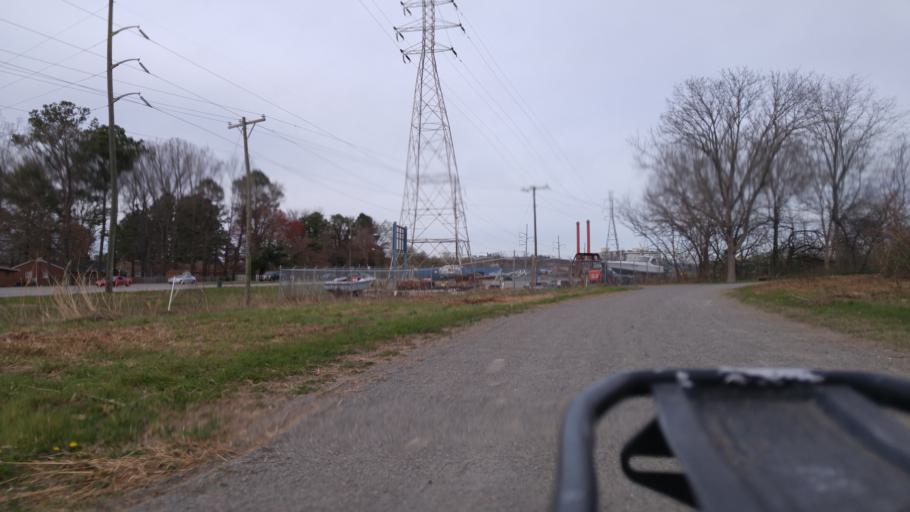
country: US
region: Virginia
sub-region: City of Portsmouth
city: Portsmouth
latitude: 36.8003
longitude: -76.3088
